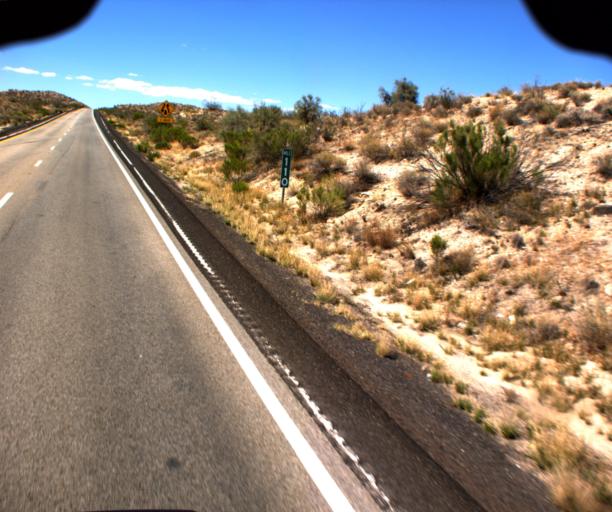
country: US
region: Arizona
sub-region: Mohave County
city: Kingman
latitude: 34.8975
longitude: -113.6538
